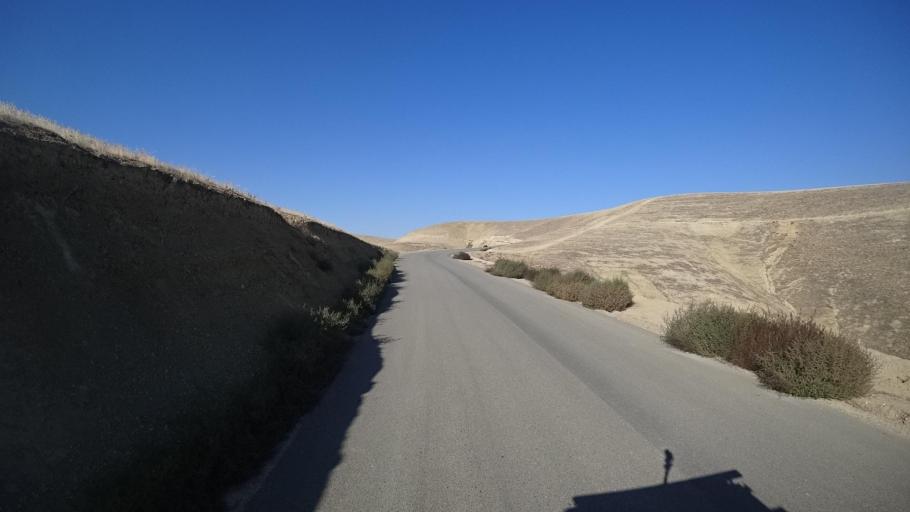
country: US
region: California
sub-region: Kern County
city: Oildale
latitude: 35.4680
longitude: -118.8706
